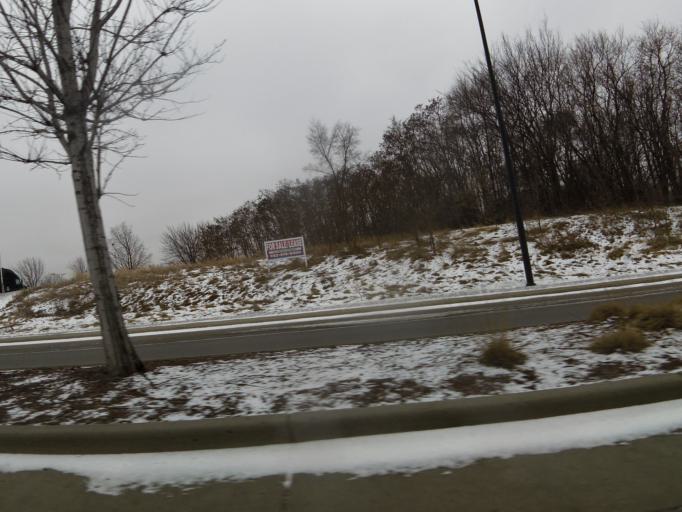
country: US
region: Minnesota
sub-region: Wright County
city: Delano
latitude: 45.0356
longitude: -93.7690
